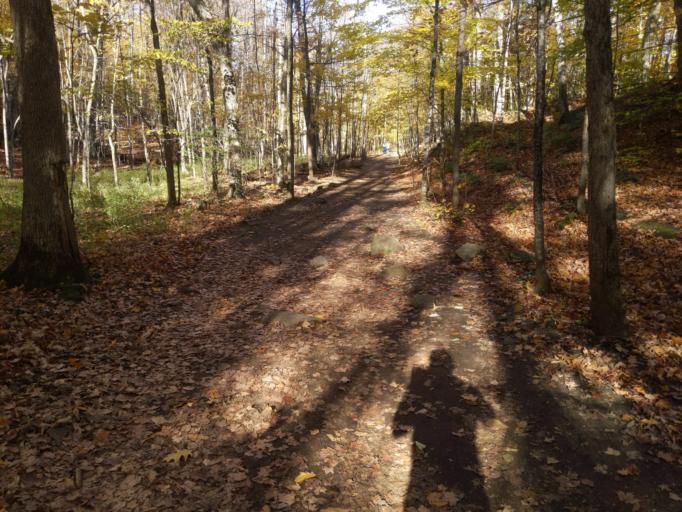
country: CA
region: Quebec
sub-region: Outaouais
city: Wakefield
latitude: 45.5367
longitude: -75.8697
